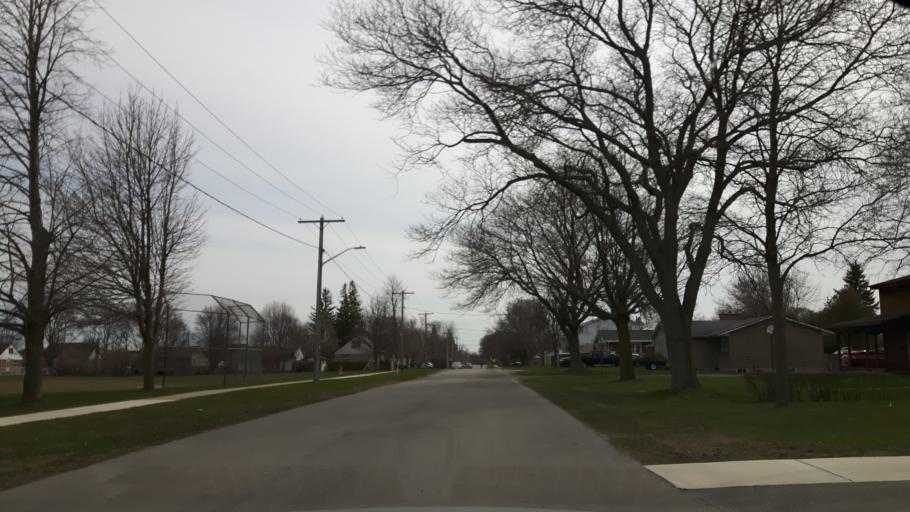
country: CA
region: Ontario
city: Goderich
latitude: 43.7369
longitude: -81.7087
